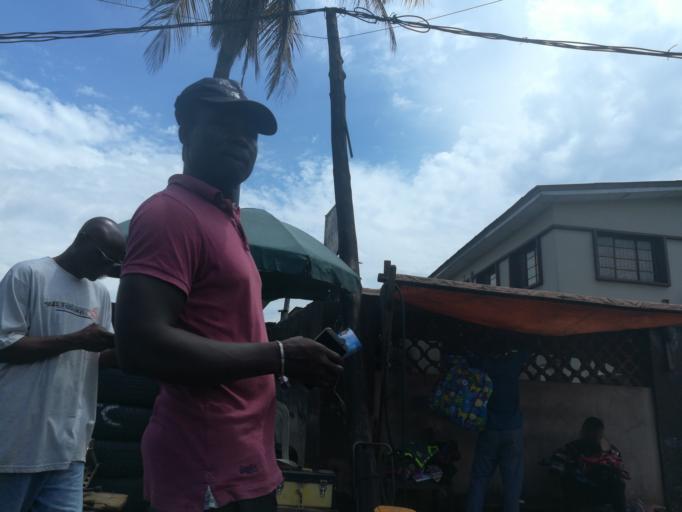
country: NG
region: Lagos
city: Ojota
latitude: 6.5637
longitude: 3.3680
